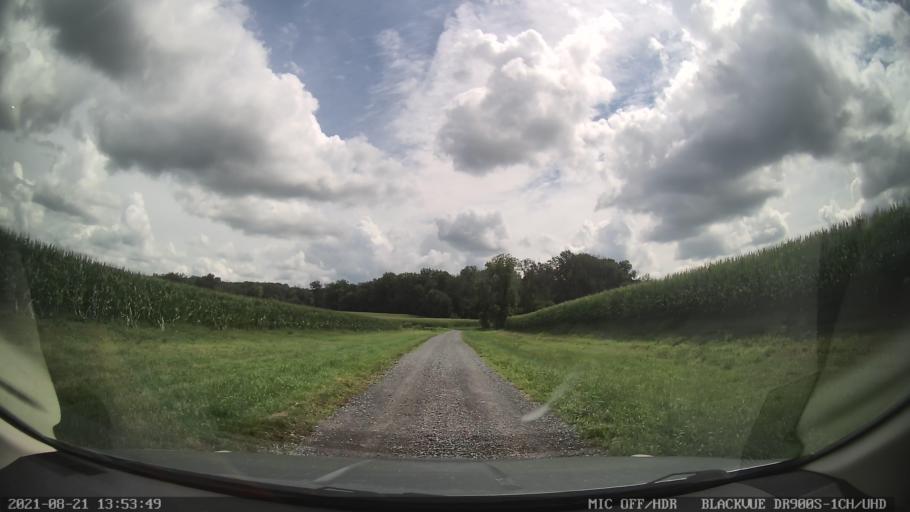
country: US
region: Pennsylvania
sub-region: Berks County
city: Fleetwood
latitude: 40.4686
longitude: -75.7791
